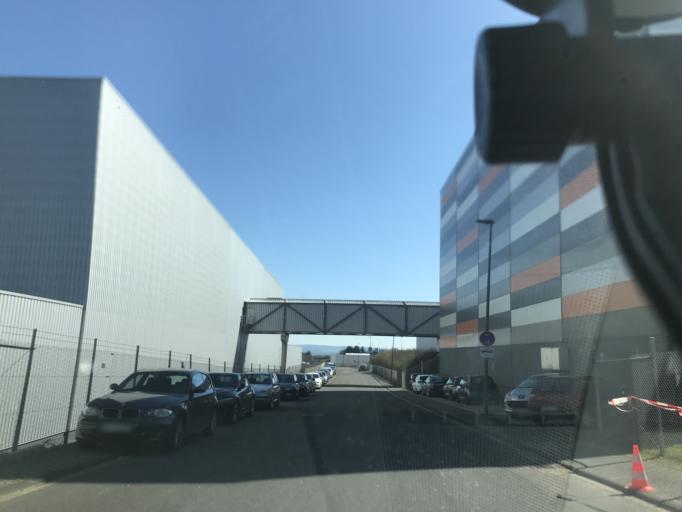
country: DE
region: Rheinland-Pfalz
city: Aach
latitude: 49.7752
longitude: 6.5857
